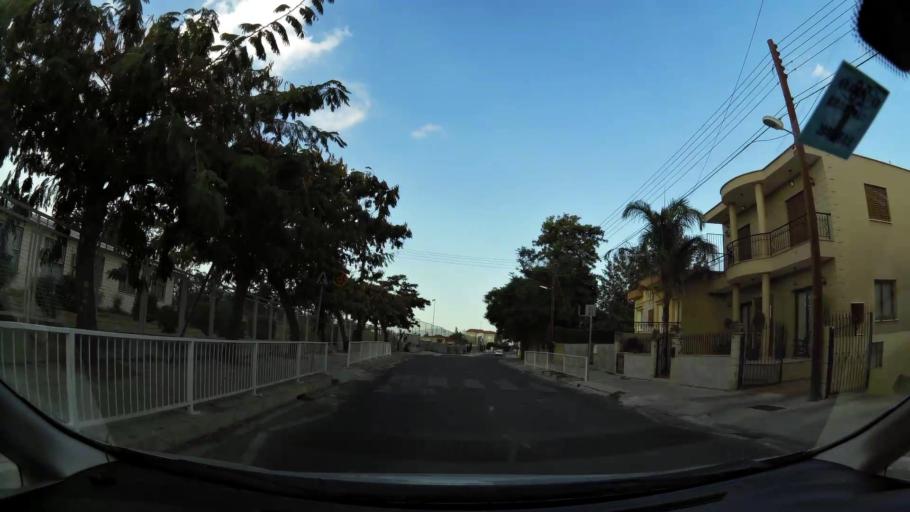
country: CY
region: Lefkosia
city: Kato Deftera
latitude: 35.1170
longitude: 33.2994
